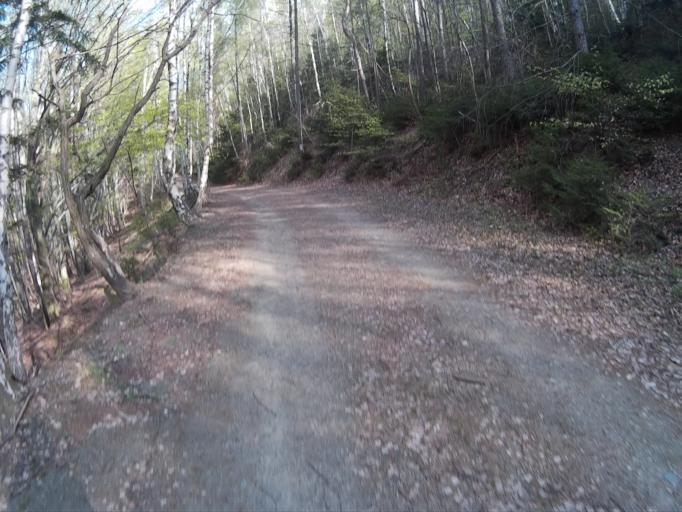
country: AT
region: Burgenland
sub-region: Politischer Bezirk Oberwart
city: Rechnitz
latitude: 47.3392
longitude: 16.4507
